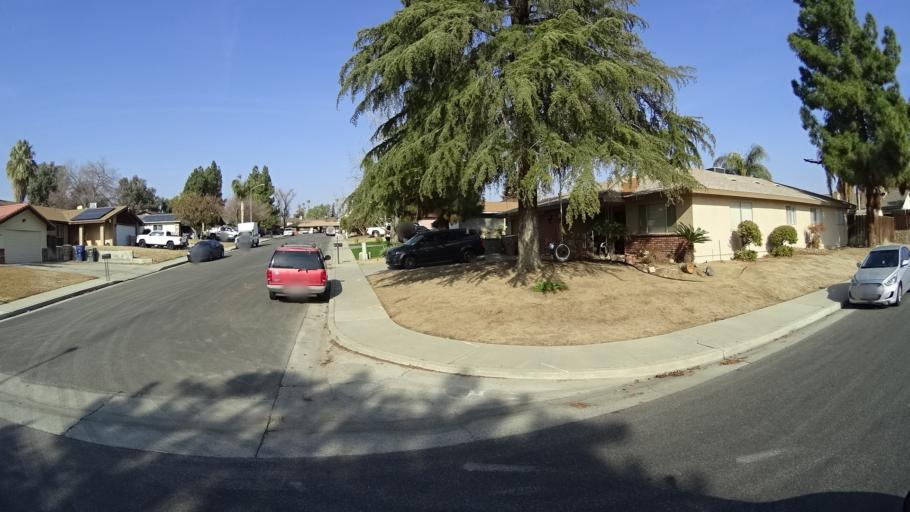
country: US
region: California
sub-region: Kern County
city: Bakersfield
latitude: 35.3871
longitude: -118.9603
